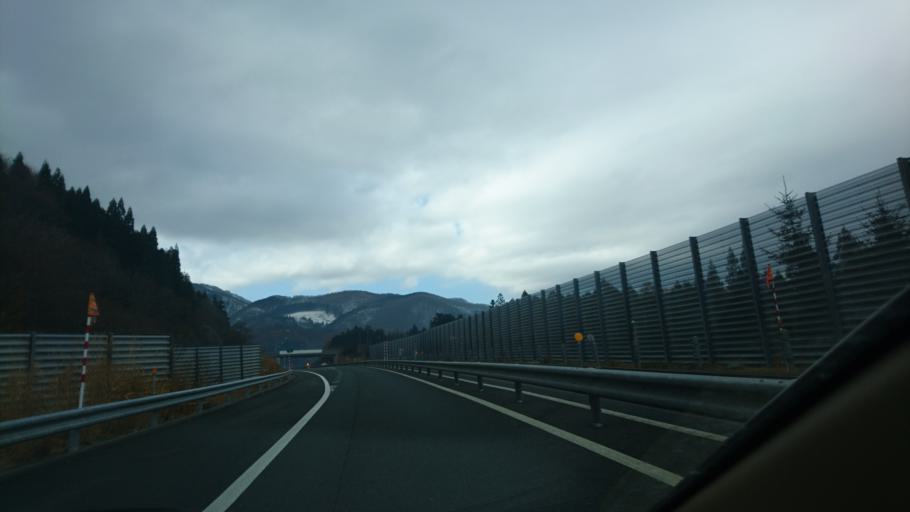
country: JP
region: Iwate
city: Kitakami
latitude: 39.2976
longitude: 140.9369
